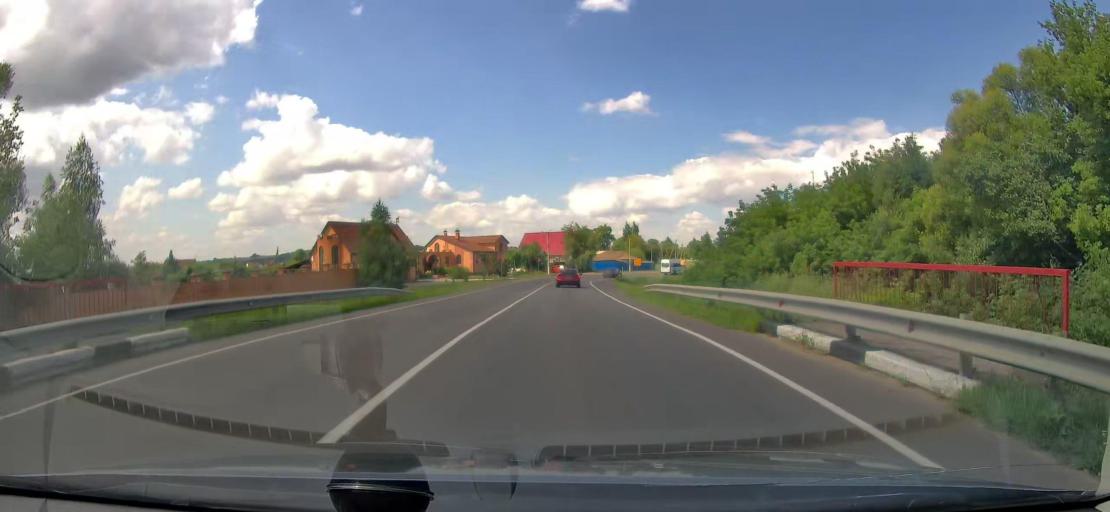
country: RU
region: Kursk
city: Zolotukhino
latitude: 51.9250
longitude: 36.3055
